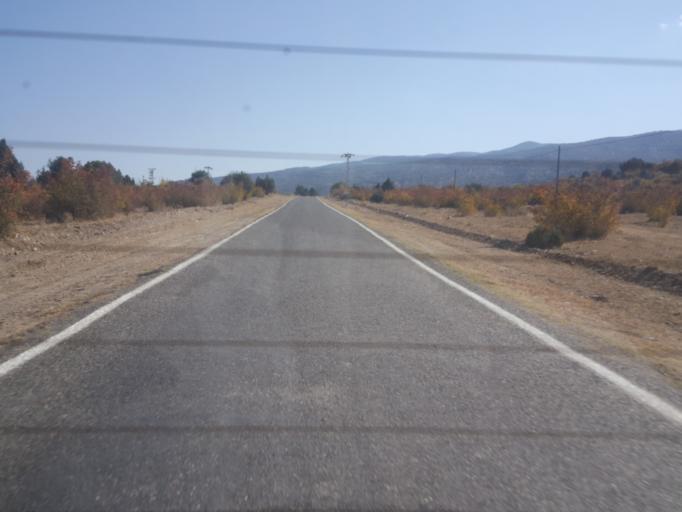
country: TR
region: Kastamonu
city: Tosya
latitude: 41.0015
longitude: 34.1509
